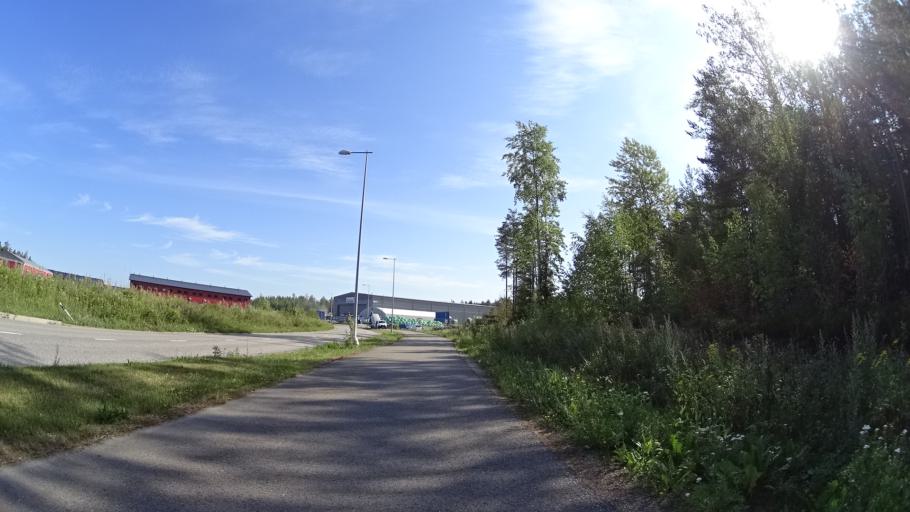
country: FI
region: Uusimaa
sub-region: Helsinki
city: Kilo
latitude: 60.2883
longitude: 24.7646
